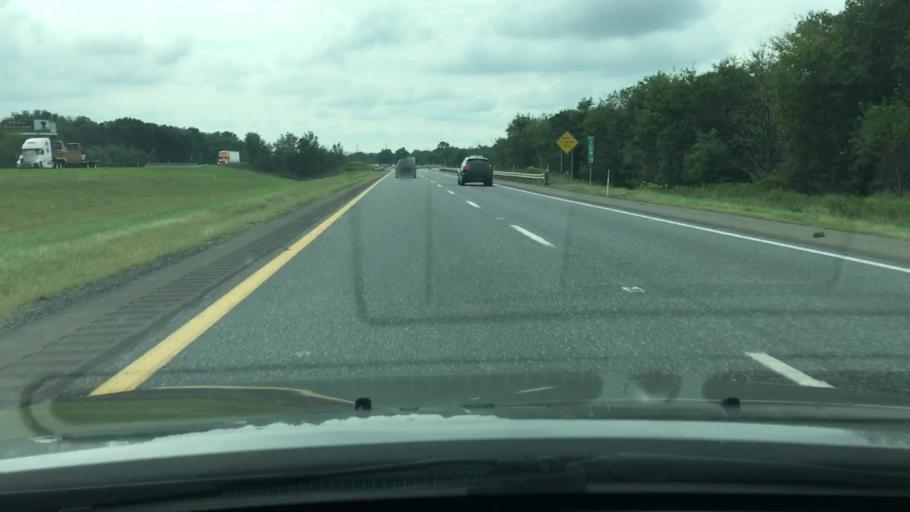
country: US
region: Pennsylvania
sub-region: Schuylkill County
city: Tremont
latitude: 40.6478
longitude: -76.4192
